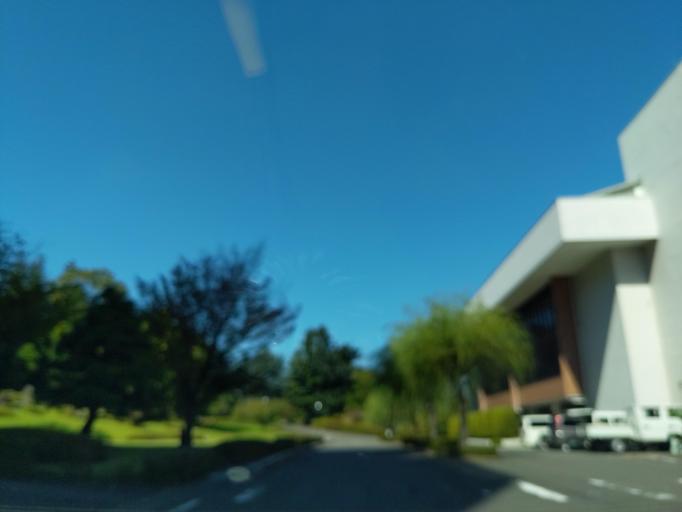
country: JP
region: Fukushima
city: Koriyama
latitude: 37.4177
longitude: 140.3747
